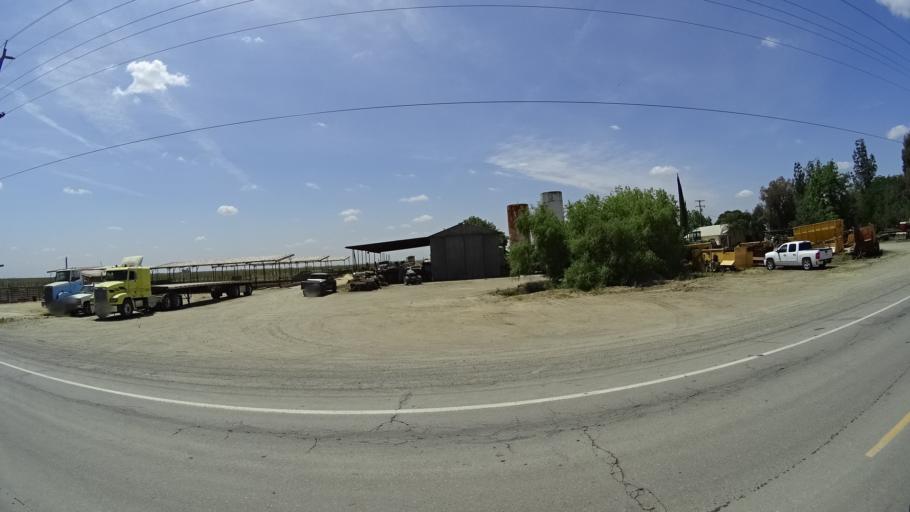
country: US
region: California
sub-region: Kings County
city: Home Garden
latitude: 36.2990
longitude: -119.5275
